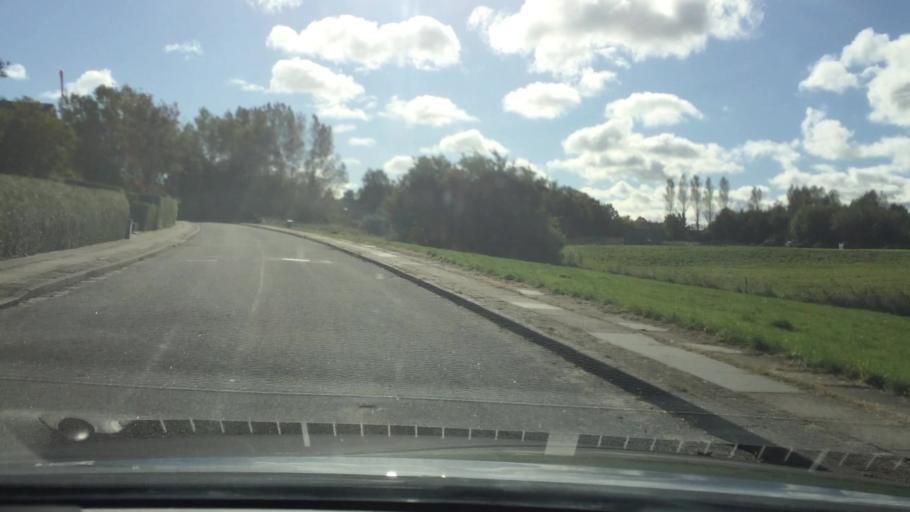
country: DK
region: Central Jutland
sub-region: Horsens Kommune
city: Horsens
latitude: 55.8777
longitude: 9.9142
